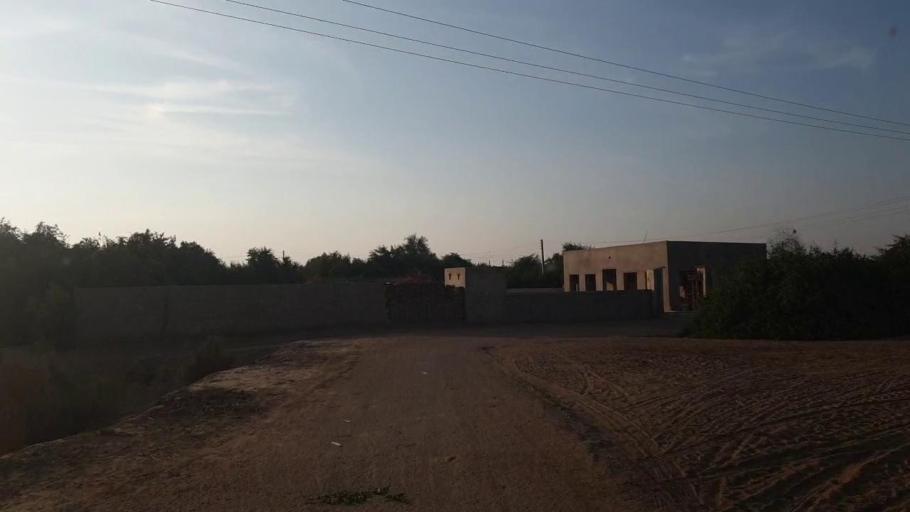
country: PK
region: Sindh
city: Sann
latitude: 25.9264
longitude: 68.1741
